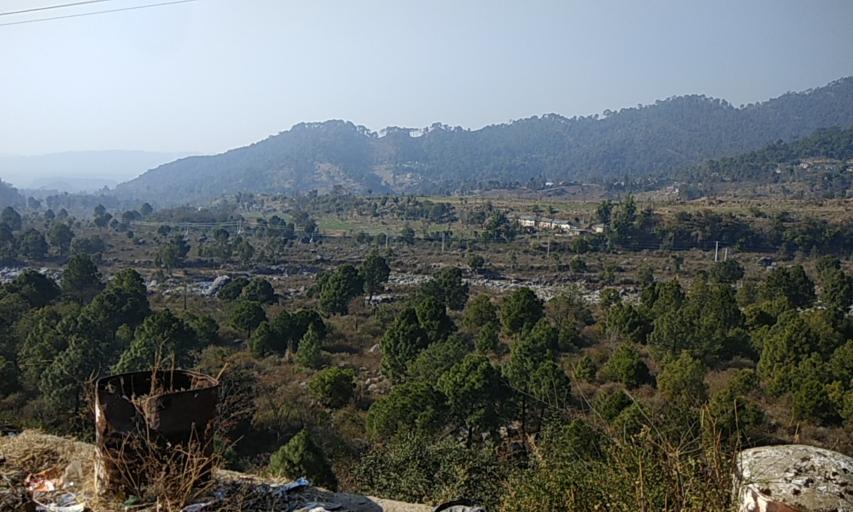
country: IN
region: Himachal Pradesh
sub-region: Kangra
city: Palampur
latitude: 32.1198
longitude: 76.5253
